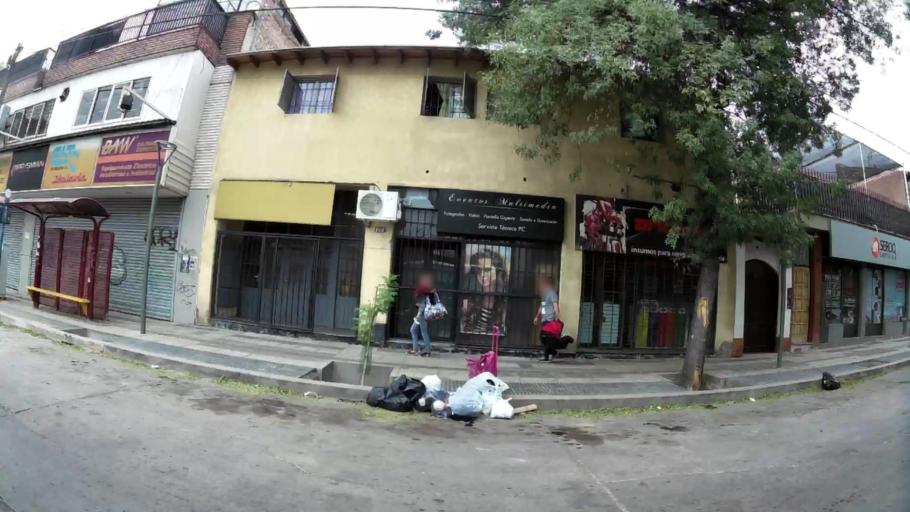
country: AR
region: Mendoza
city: Mendoza
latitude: -32.8825
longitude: -68.8328
